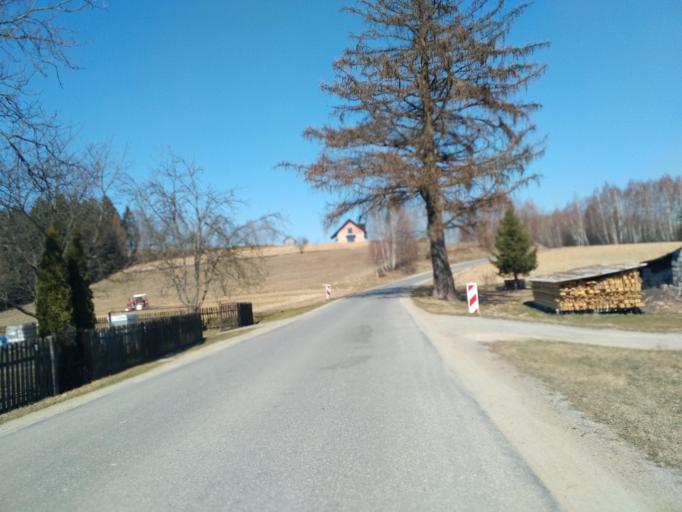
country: PL
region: Subcarpathian Voivodeship
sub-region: Powiat debicki
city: Brzostek
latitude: 49.9528
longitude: 21.4292
